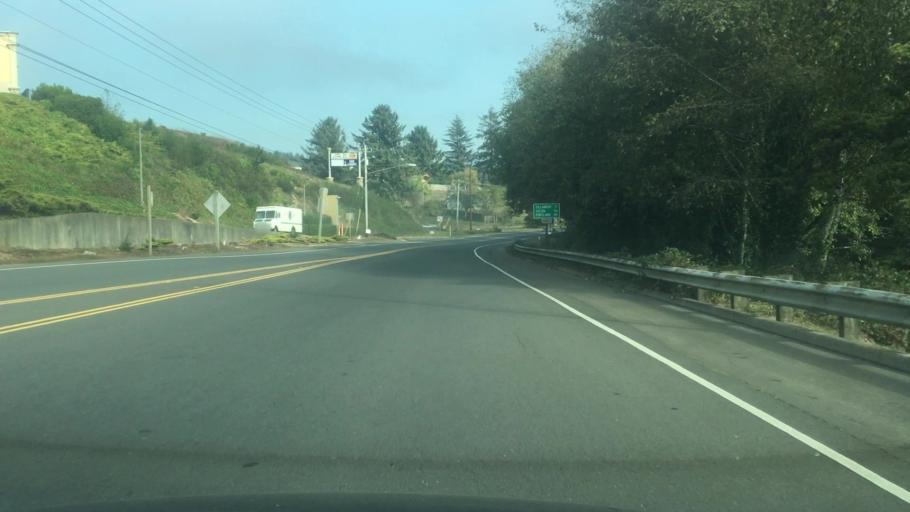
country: US
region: Oregon
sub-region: Lincoln County
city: Lincoln City
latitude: 44.9964
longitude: -124.0034
